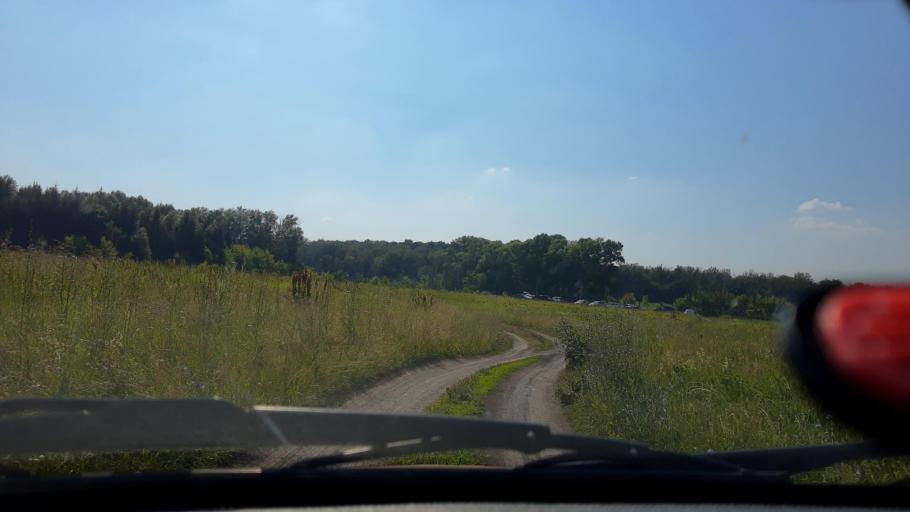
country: RU
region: Bashkortostan
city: Kabakovo
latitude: 54.7462
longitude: 56.1805
